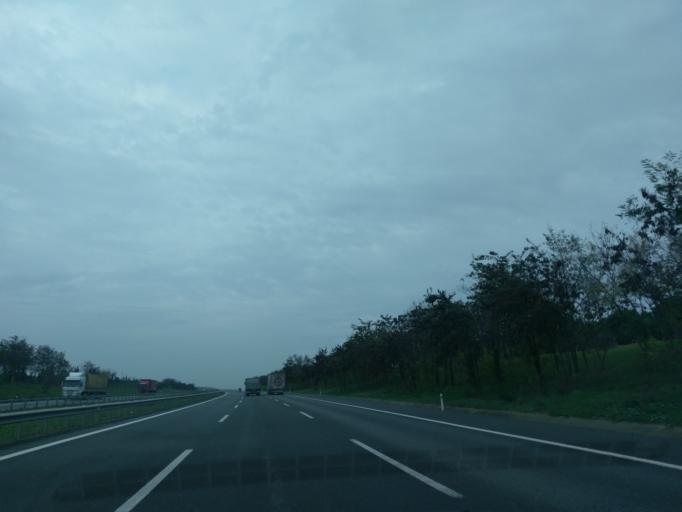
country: TR
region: Istanbul
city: Canta
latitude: 41.1622
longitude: 28.1339
